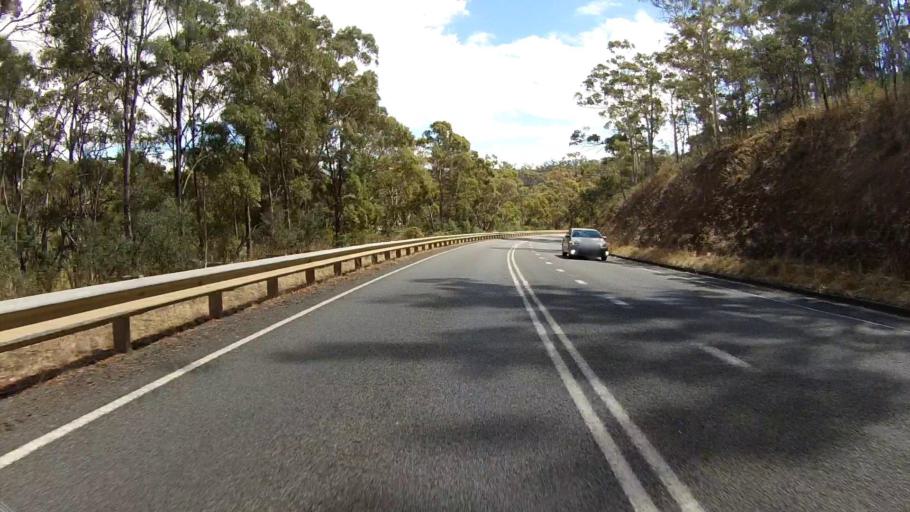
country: AU
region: Tasmania
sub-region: Sorell
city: Sorell
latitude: -42.6105
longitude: 147.6456
